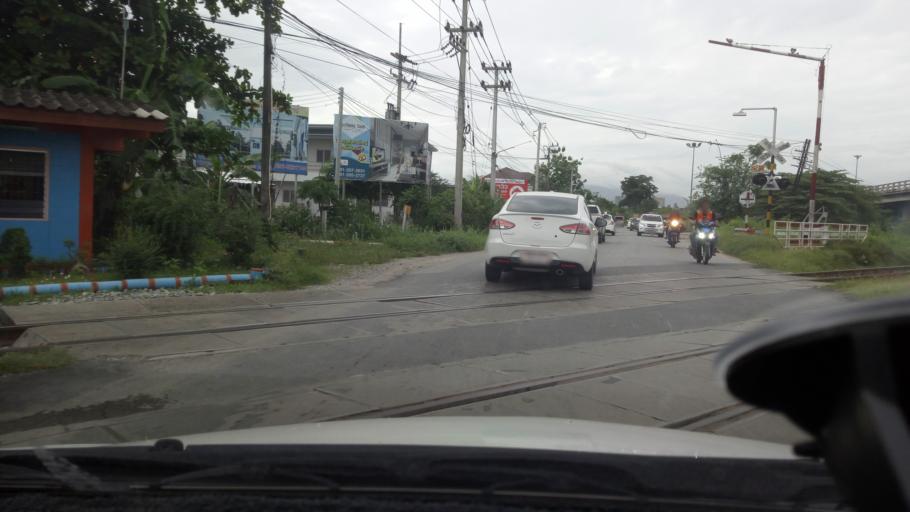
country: TH
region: Chon Buri
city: Chon Buri
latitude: 13.4040
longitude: 101.0480
